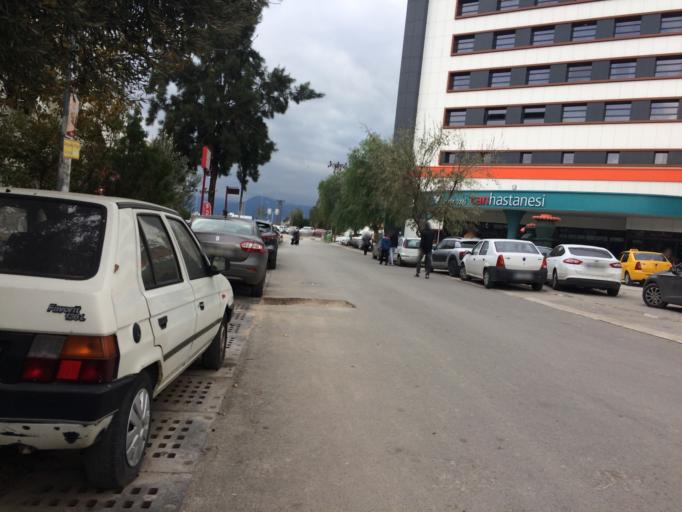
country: TR
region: Izmir
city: Karsiyaka
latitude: 38.4834
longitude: 27.0589
